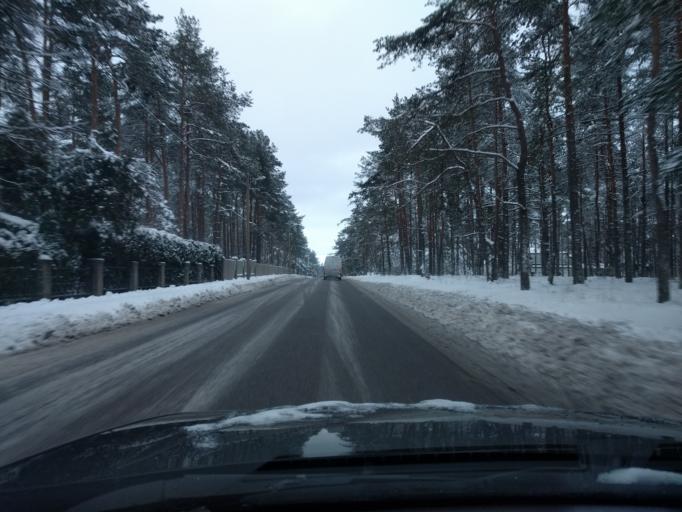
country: EE
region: Harju
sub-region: Saue vald
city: Laagri
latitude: 59.3766
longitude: 24.6714
